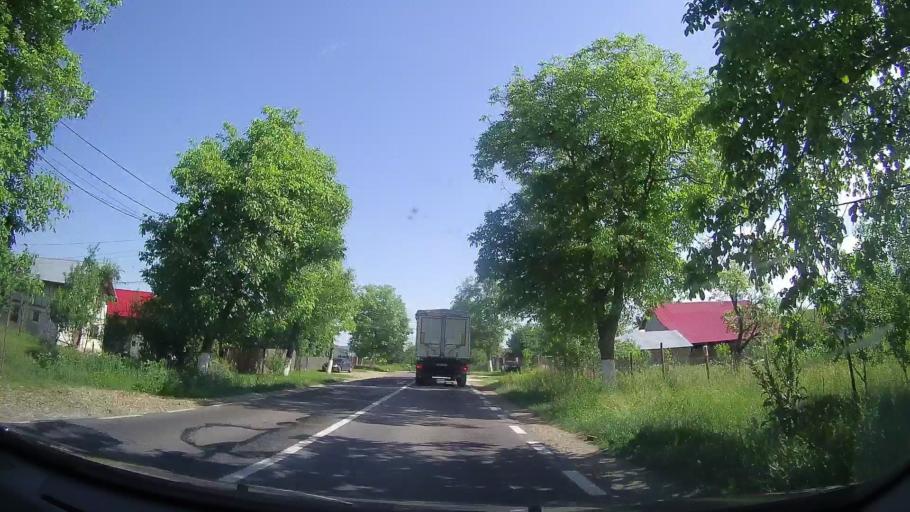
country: RO
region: Prahova
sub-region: Comuna Izvoarele
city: Homoraciu
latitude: 45.2412
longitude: 26.0278
